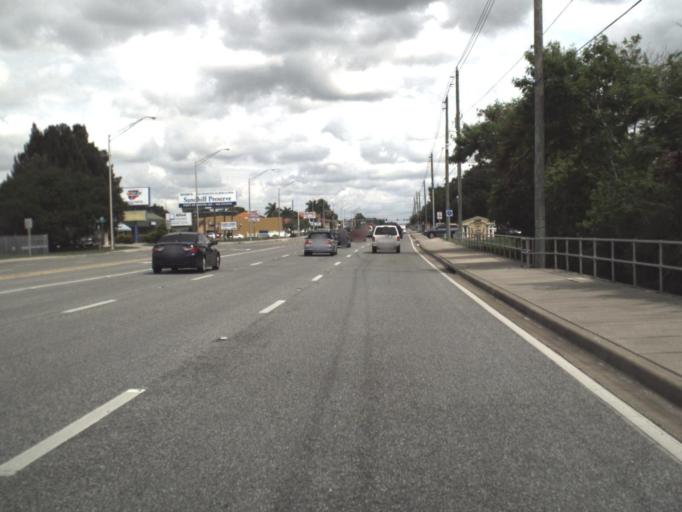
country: US
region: Florida
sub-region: Sarasota County
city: South Gate Ridge
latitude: 27.2692
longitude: -82.4946
